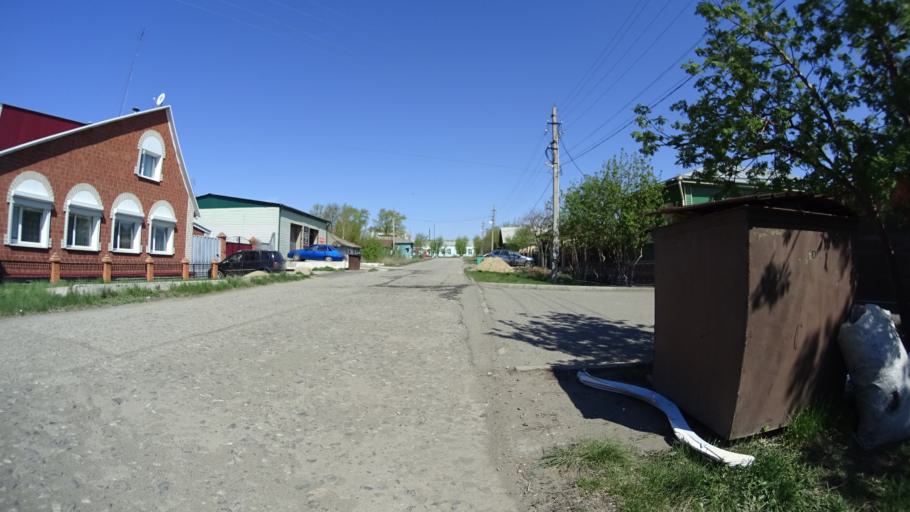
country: RU
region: Chelyabinsk
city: Troitsk
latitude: 54.0944
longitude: 61.5876
